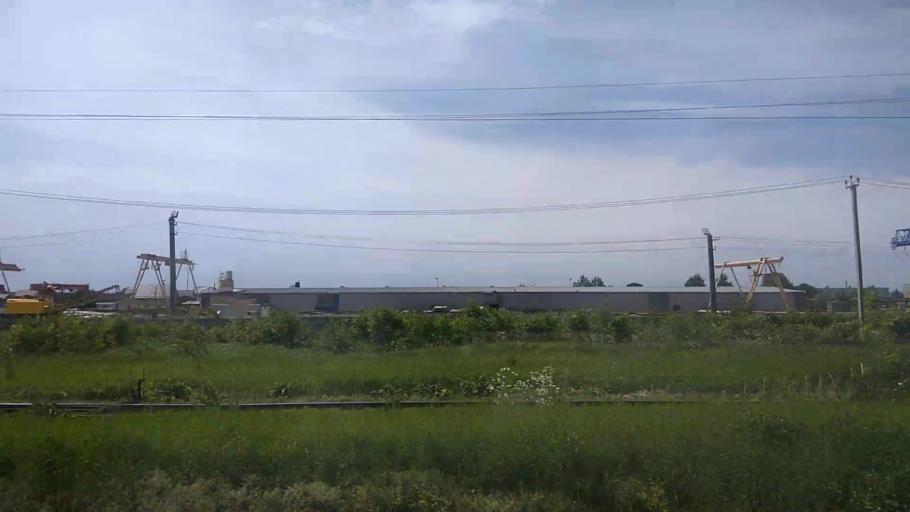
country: RU
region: Moskovskaya
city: Malyshevo
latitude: 55.5063
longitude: 38.3504
